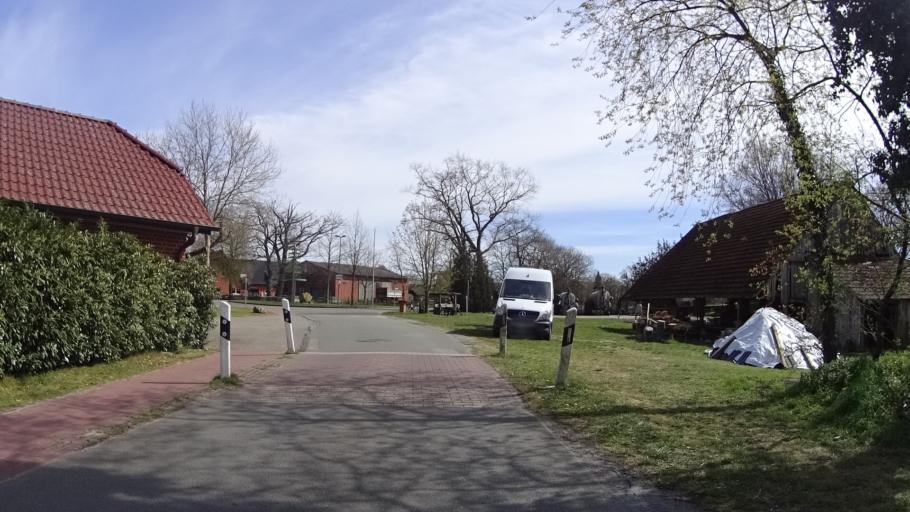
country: DE
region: Lower Saxony
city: Spelle
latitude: 52.3577
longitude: 7.4419
